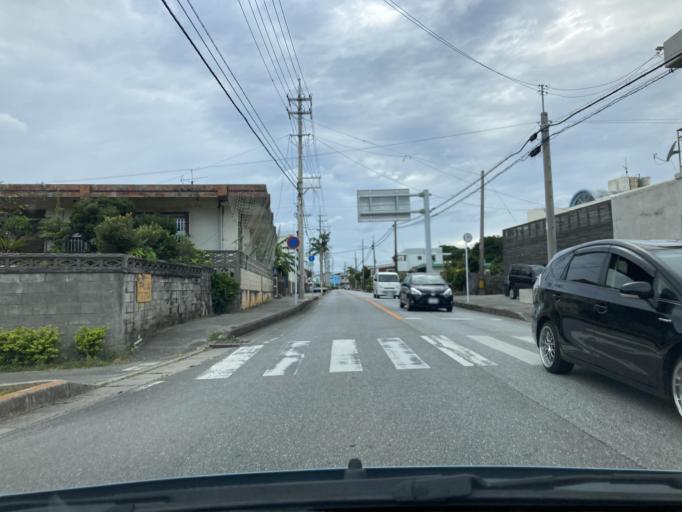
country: JP
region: Okinawa
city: Ishikawa
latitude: 26.4374
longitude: 127.7784
